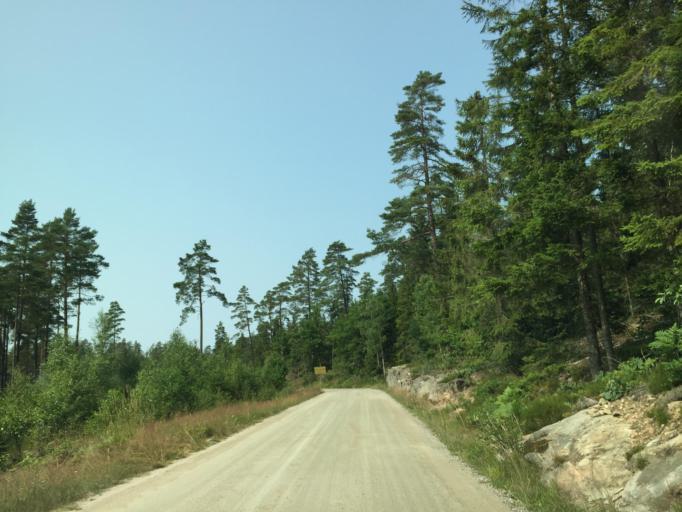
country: SE
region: Vaestra Goetaland
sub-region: Lilla Edets Kommun
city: Lilla Edet
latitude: 58.2318
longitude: 12.1127
